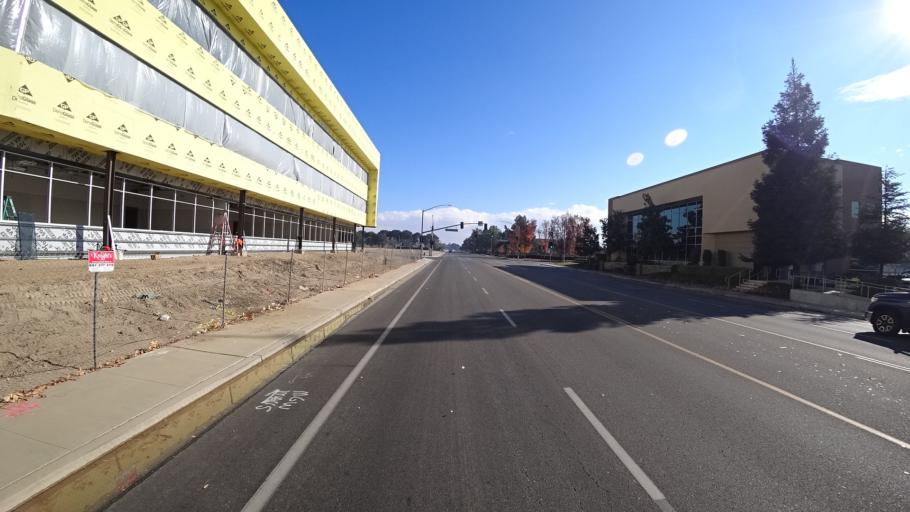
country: US
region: California
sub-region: Kern County
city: Greenacres
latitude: 35.3430
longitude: -119.1070
